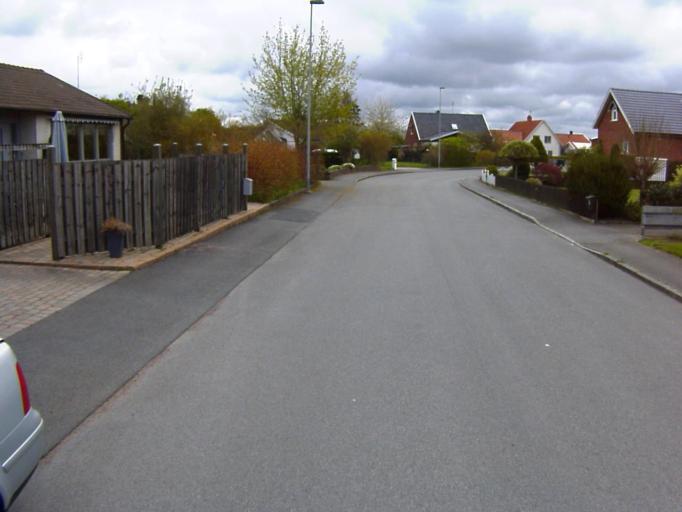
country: SE
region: Skane
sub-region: Kristianstads Kommun
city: Kristianstad
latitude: 56.0522
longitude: 14.1756
